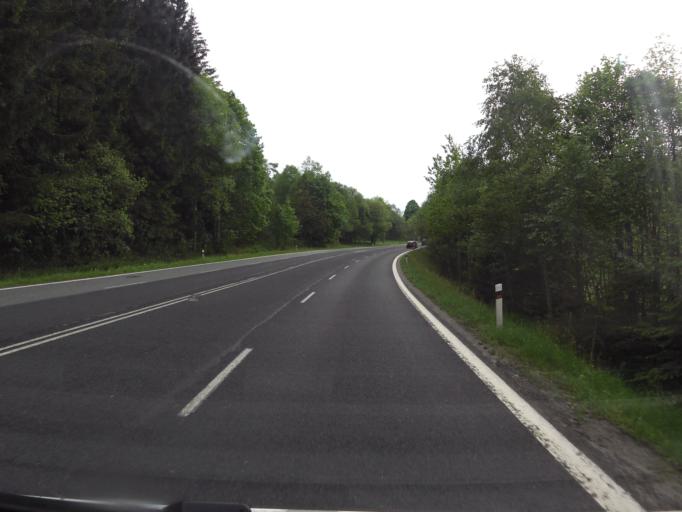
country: DE
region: Bavaria
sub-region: Lower Bavaria
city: Philippsreut
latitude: 48.8862
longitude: 13.7080
